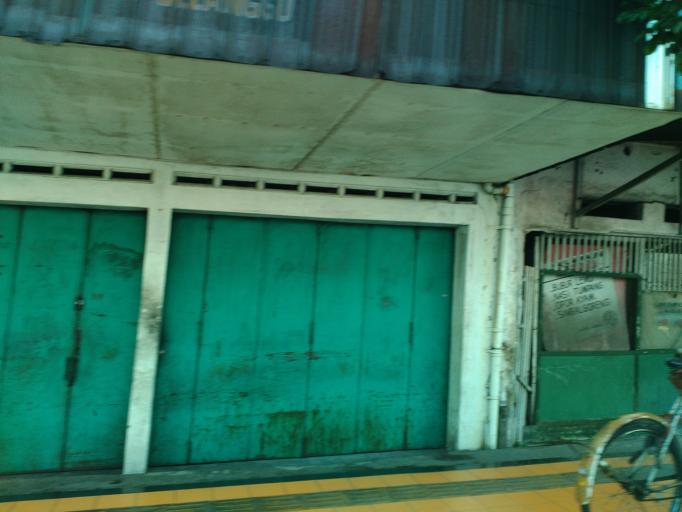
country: ID
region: Central Java
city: Delanggu
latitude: -7.6201
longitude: 110.6991
